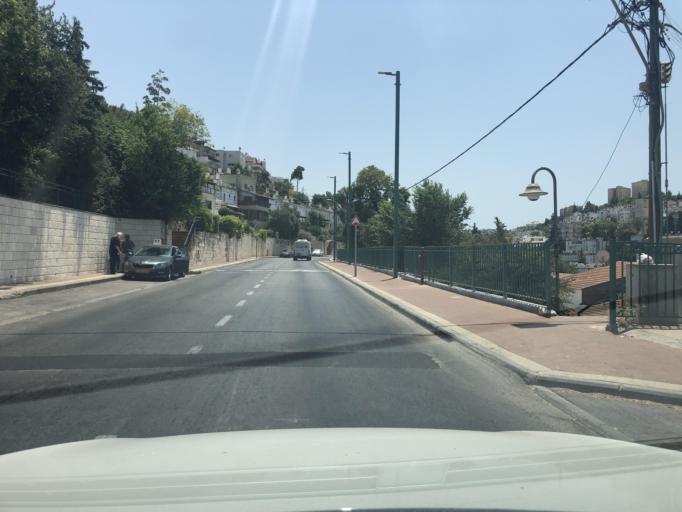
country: IL
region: Haifa
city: Daliyat el Karmil
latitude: 32.6582
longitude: 35.1079
